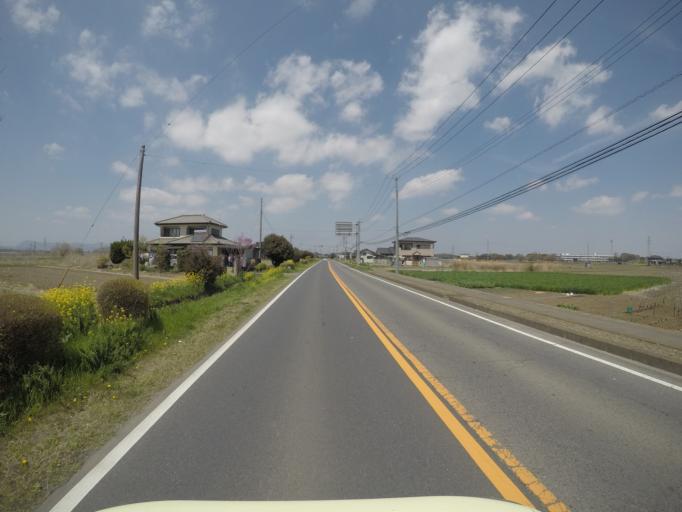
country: JP
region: Tochigi
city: Mibu
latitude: 36.4333
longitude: 139.7932
